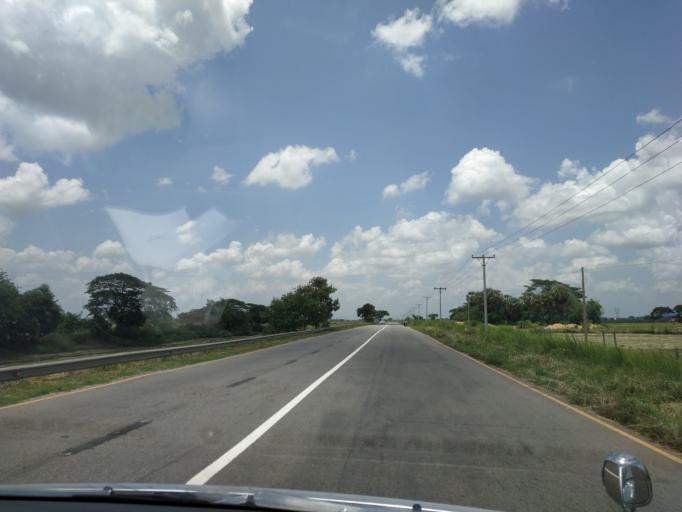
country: MM
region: Bago
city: Thanatpin
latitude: 17.4993
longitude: 96.6965
